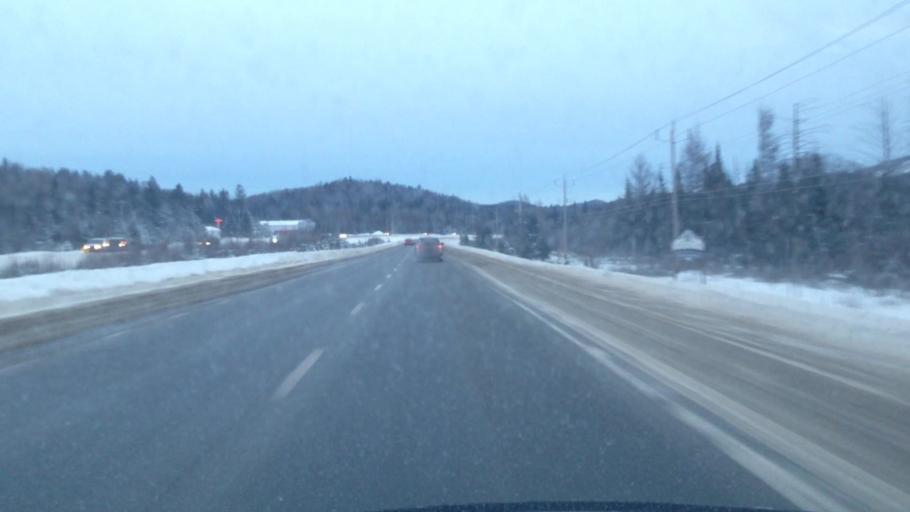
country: CA
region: Quebec
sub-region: Laurentides
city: Mont-Tremblant
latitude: 46.1120
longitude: -74.5274
